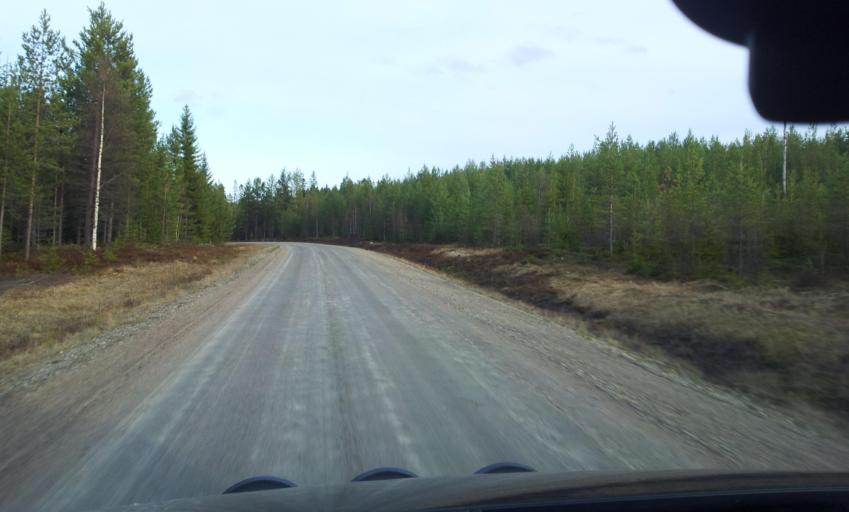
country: SE
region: Gaevleborg
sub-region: Ljusdals Kommun
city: Farila
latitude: 62.1155
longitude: 15.6897
